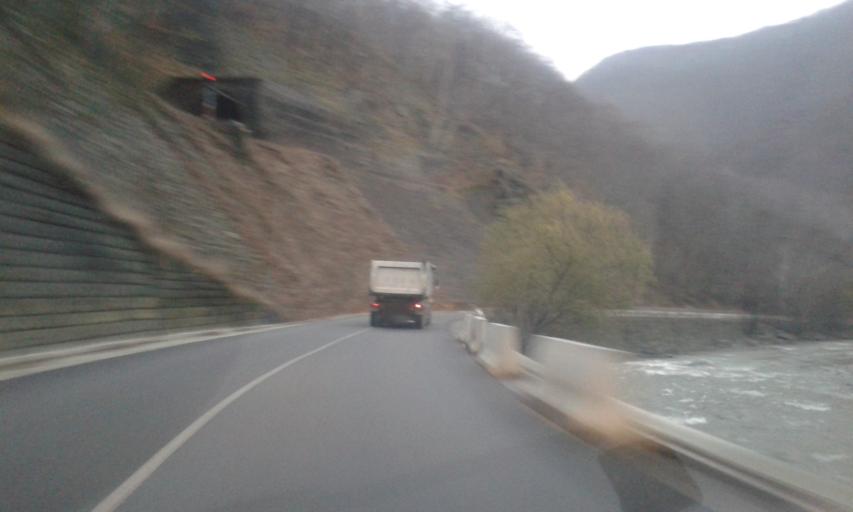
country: RO
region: Gorj
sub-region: Comuna Bumbesti-Jiu
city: Bumbesti-Jiu
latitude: 45.2268
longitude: 23.3886
